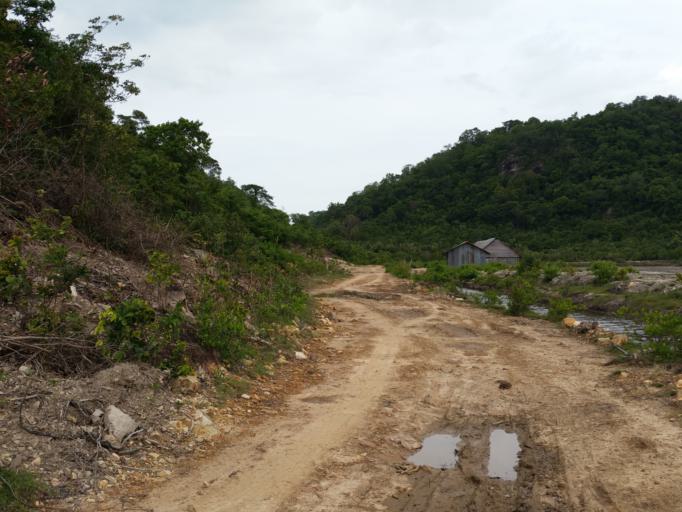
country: KH
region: Kampot
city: Kampot
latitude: 10.5554
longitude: 104.1733
